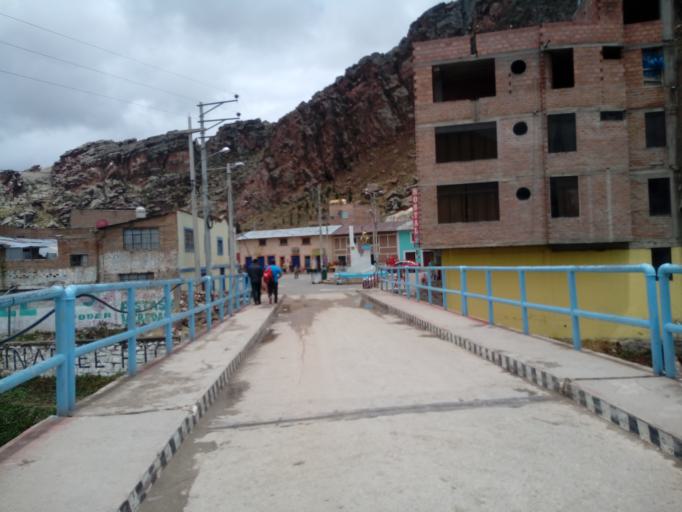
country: PE
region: Puno
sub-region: San Antonio De Putina
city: Putina
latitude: -14.9159
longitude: -69.8673
